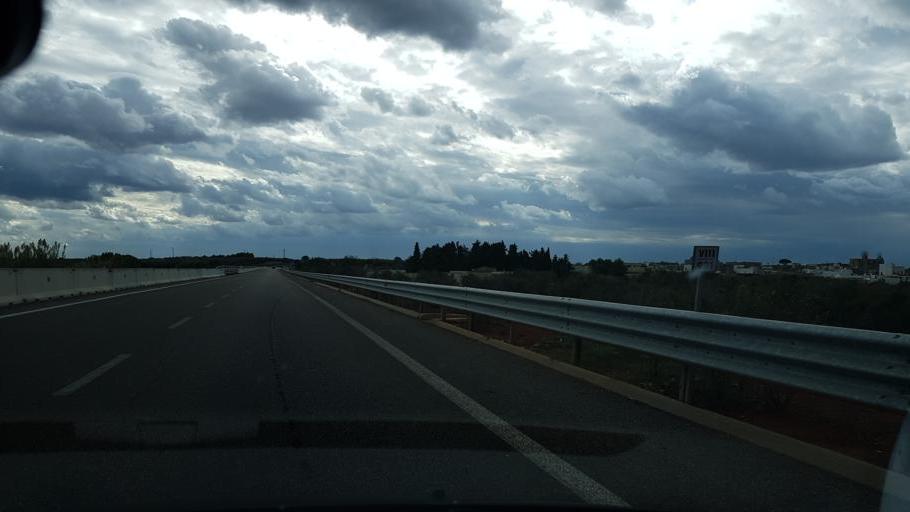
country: IT
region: Apulia
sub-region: Provincia di Lecce
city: Palmariggi
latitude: 40.1315
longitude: 18.3898
